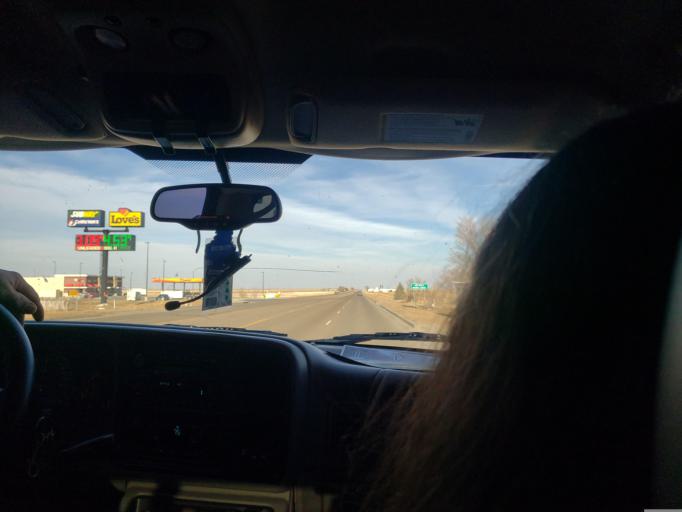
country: US
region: Oklahoma
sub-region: Texas County
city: Goodwell
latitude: 36.5044
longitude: -101.7754
